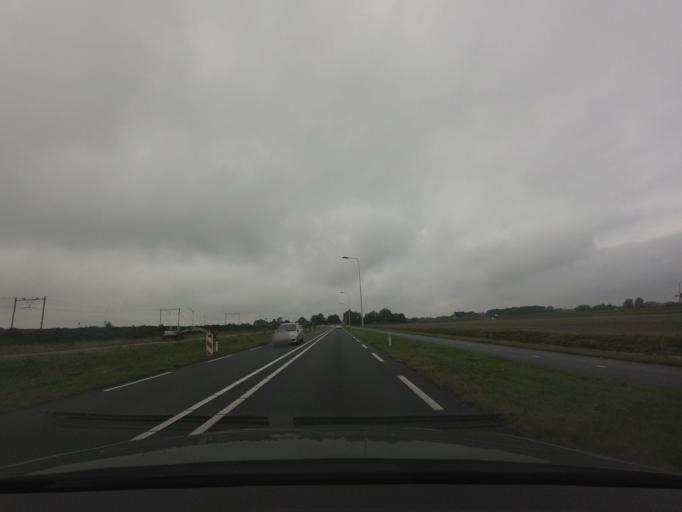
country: NL
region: North Holland
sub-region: Gemeente Langedijk
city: Broek op Langedijk
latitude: 52.6634
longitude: 4.8058
